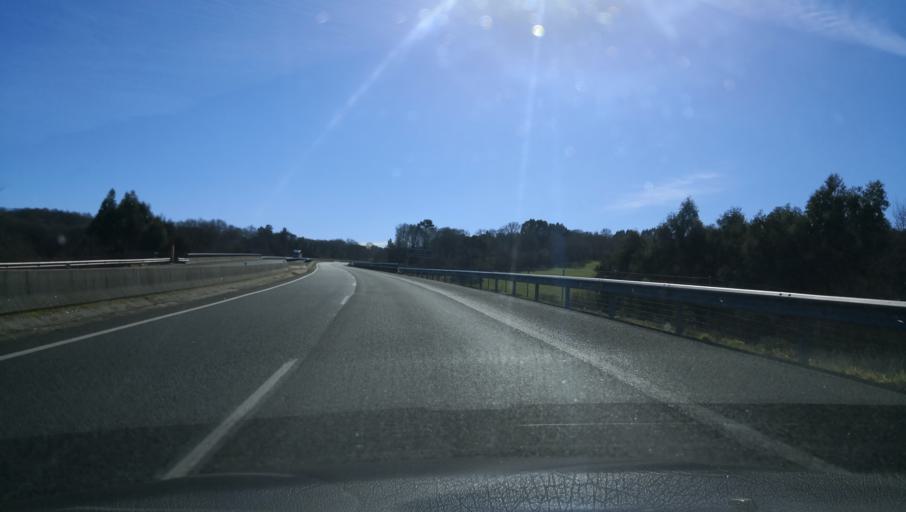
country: ES
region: Galicia
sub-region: Provincia de Pontevedra
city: Lalin
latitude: 42.6622
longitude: -8.1456
